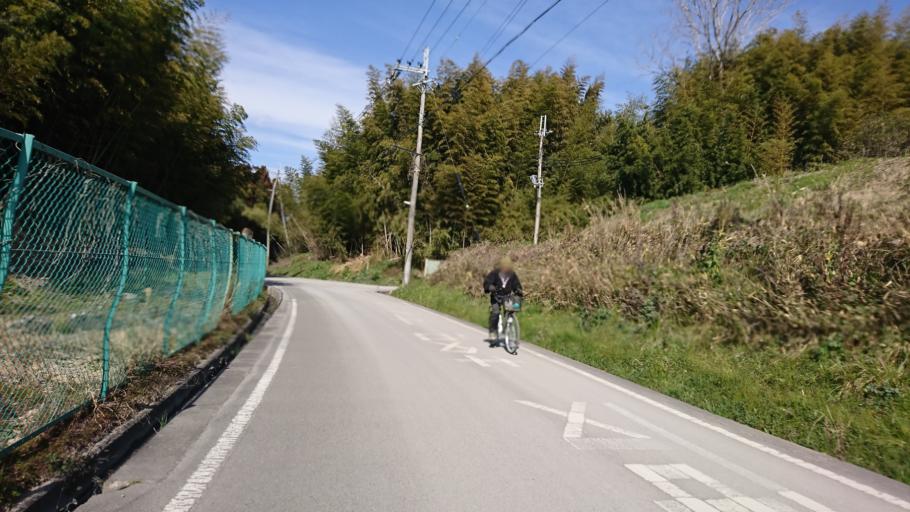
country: JP
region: Hyogo
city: Kakogawacho-honmachi
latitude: 34.8207
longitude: 134.8317
